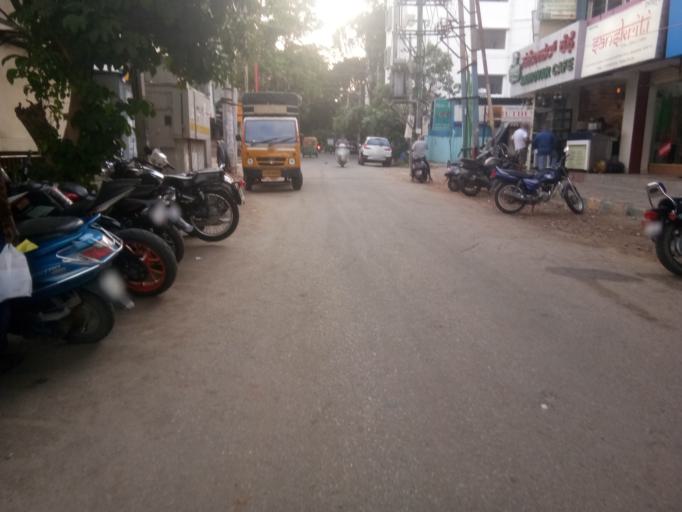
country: IN
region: Karnataka
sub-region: Bangalore Urban
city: Bangalore
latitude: 13.0144
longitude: 77.6304
